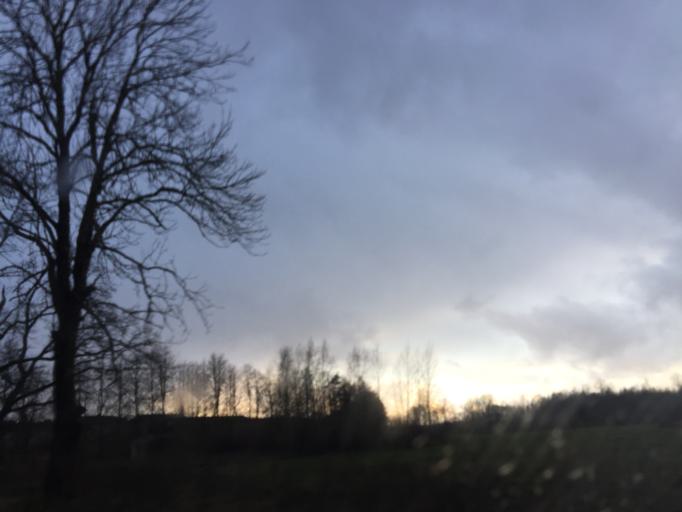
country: LV
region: Burtnieki
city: Matisi
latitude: 57.6943
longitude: 25.2636
